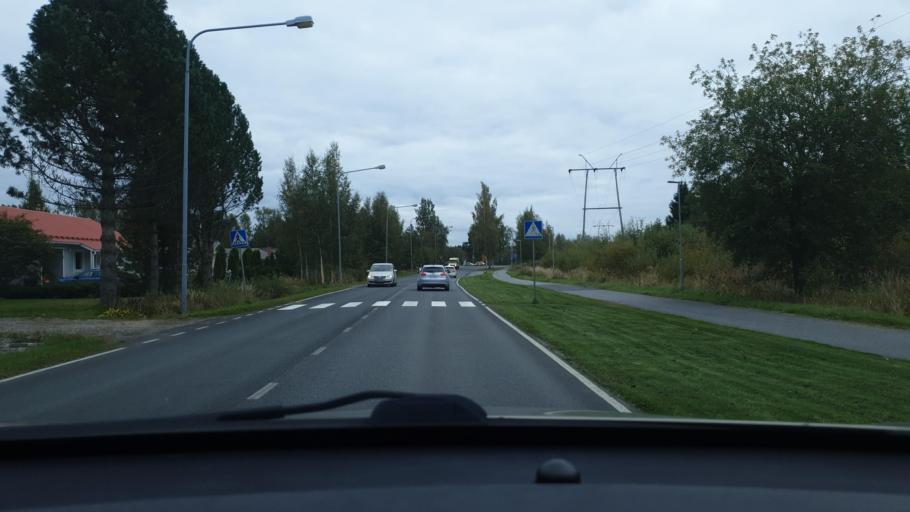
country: FI
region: Ostrobothnia
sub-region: Vaasa
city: Teeriniemi
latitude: 63.0911
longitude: 21.6990
